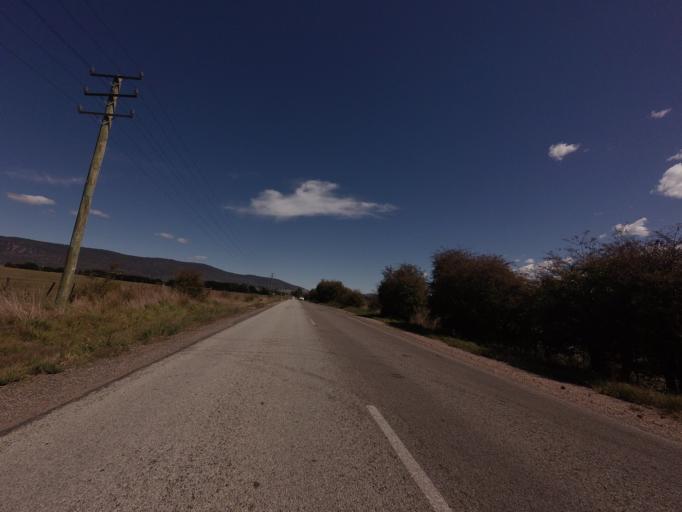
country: AU
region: Tasmania
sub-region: Break O'Day
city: St Helens
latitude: -41.6242
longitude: 147.9960
